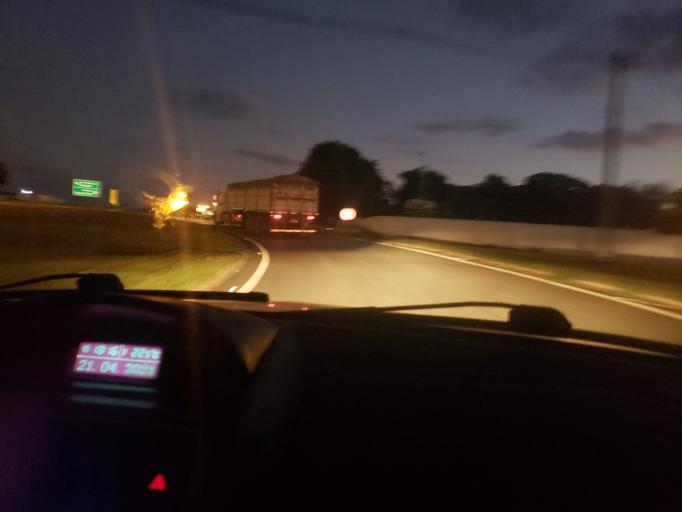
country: BR
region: Sao Paulo
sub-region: Conchal
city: Conchal
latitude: -22.3435
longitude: -47.1582
